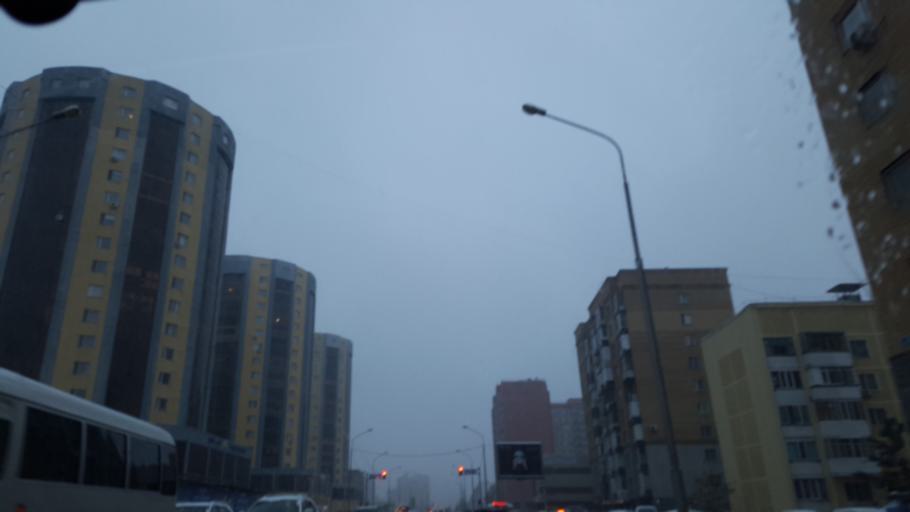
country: KZ
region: Astana Qalasy
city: Astana
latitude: 51.1583
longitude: 71.4940
